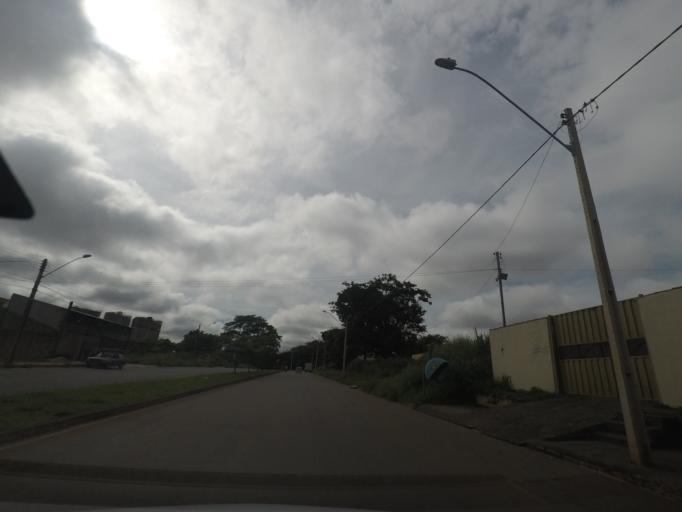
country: BR
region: Goias
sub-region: Goiania
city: Goiania
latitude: -16.7437
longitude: -49.3125
